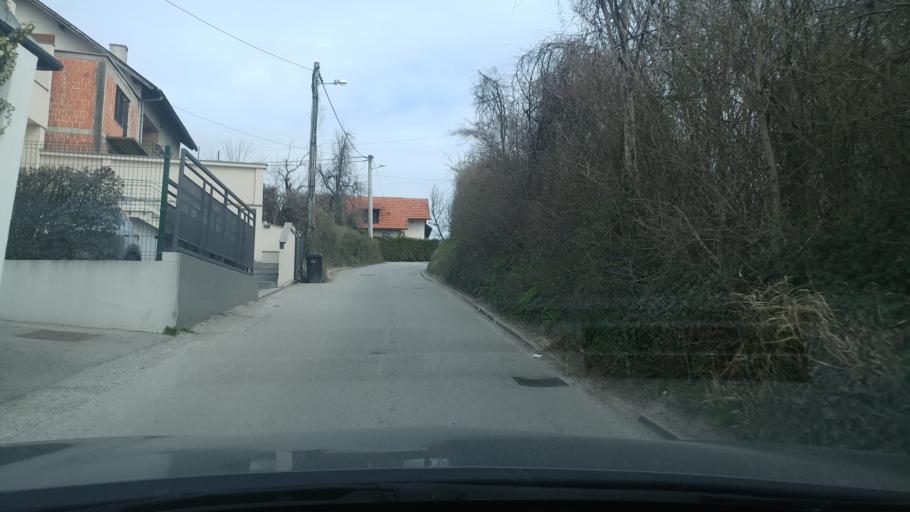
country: HR
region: Grad Zagreb
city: Stenjevec
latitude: 45.8420
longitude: 15.9247
